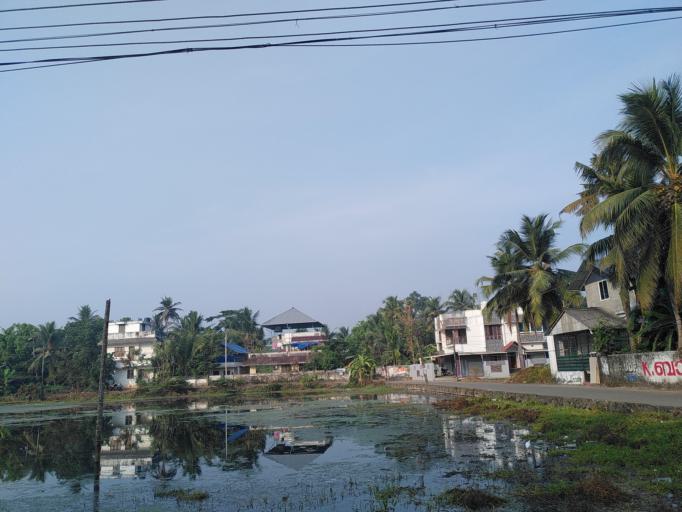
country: IN
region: Kerala
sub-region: Alappuzha
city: Arukutti
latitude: 9.9288
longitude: 76.3273
